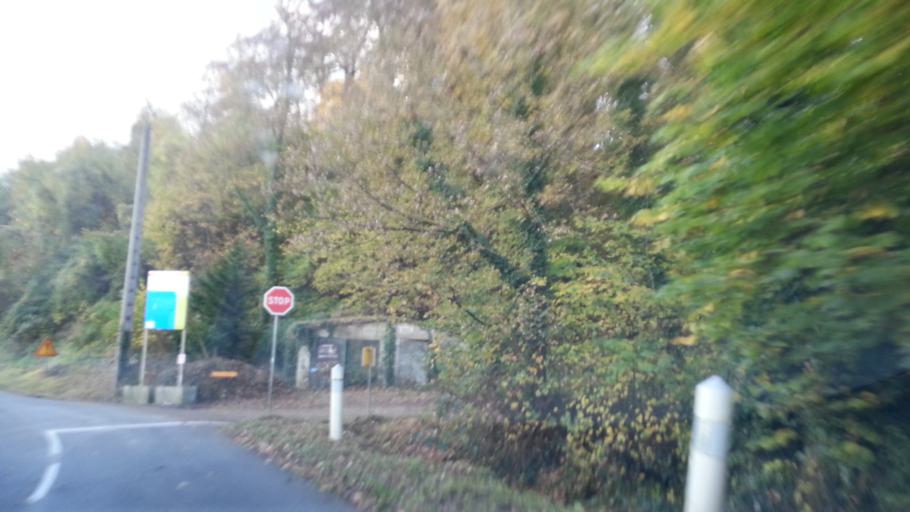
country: FR
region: Picardie
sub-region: Departement de l'Oise
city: Thiverny
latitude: 49.2581
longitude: 2.3966
